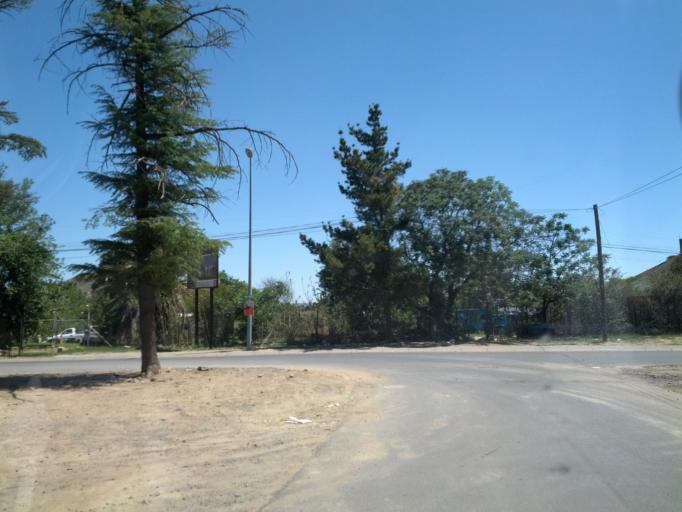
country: LS
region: Maseru
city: Maseru
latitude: -29.3138
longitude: 27.4752
